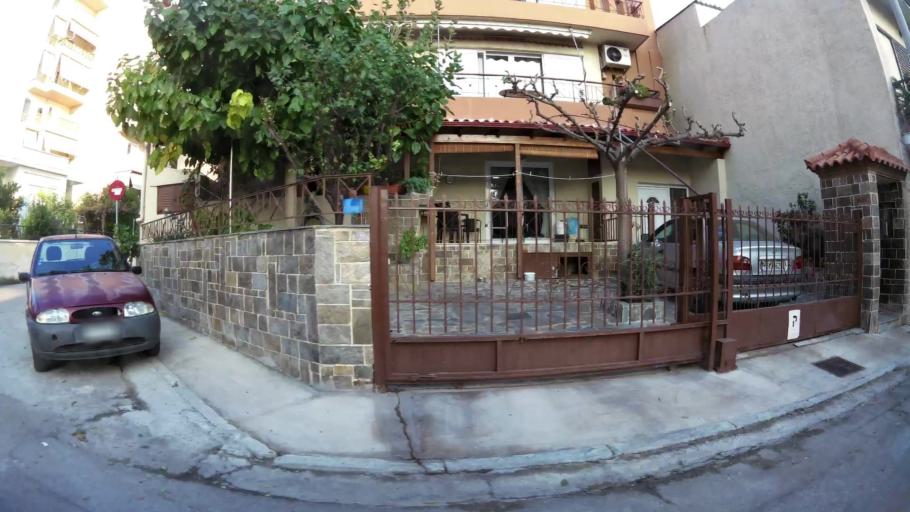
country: GR
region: Attica
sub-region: Nomarchia Anatolikis Attikis
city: Acharnes
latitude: 38.0873
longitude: 23.7347
